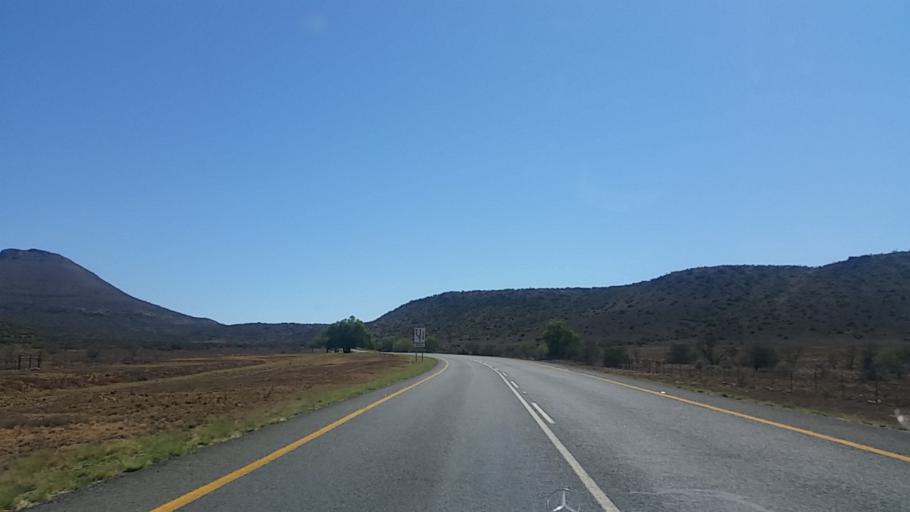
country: ZA
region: Eastern Cape
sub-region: Cacadu District Municipality
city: Graaff-Reinet
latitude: -32.0724
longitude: 24.6047
